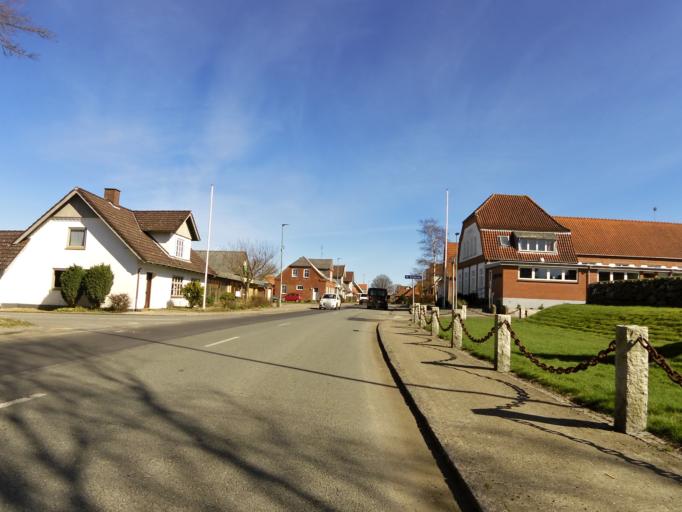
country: DK
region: South Denmark
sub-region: Vejen Kommune
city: Rodding
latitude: 55.3536
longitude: 8.9785
